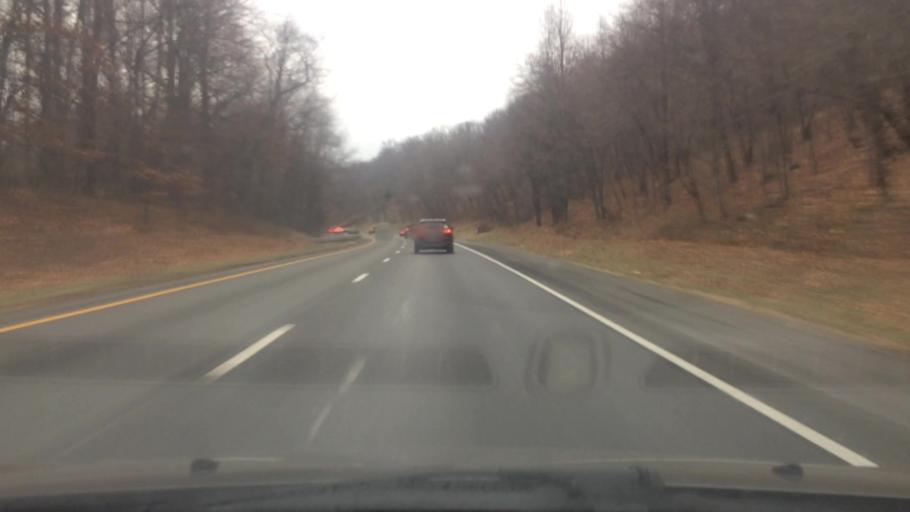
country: US
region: Maryland
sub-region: Washington County
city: Boonsboro
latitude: 39.5514
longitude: -77.6089
